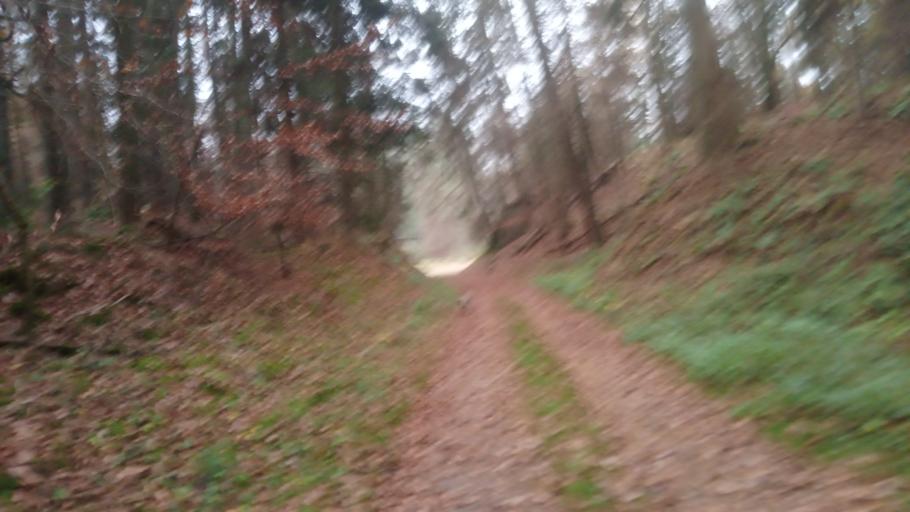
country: DE
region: North Rhine-Westphalia
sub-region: Regierungsbezirk Detmold
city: Willebadessen
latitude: 51.5074
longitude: 9.0069
